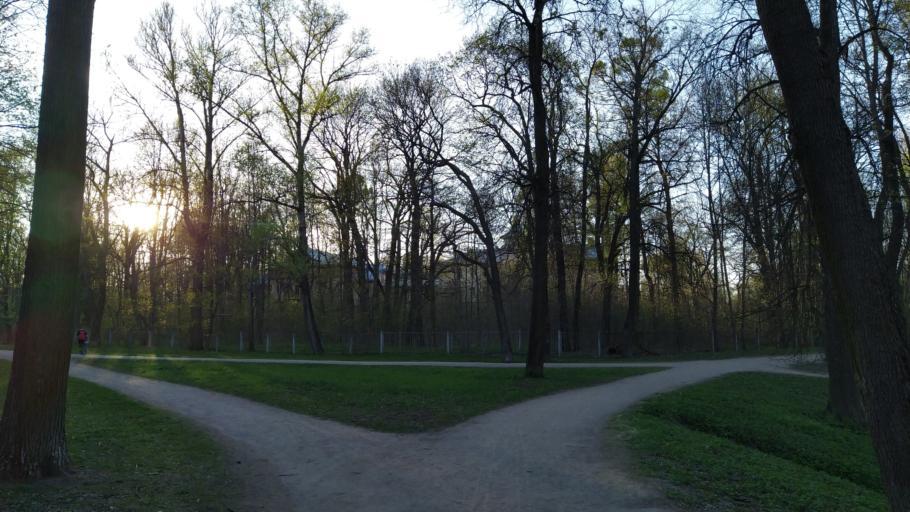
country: RU
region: St.-Petersburg
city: Pushkin
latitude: 59.7073
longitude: 30.4199
